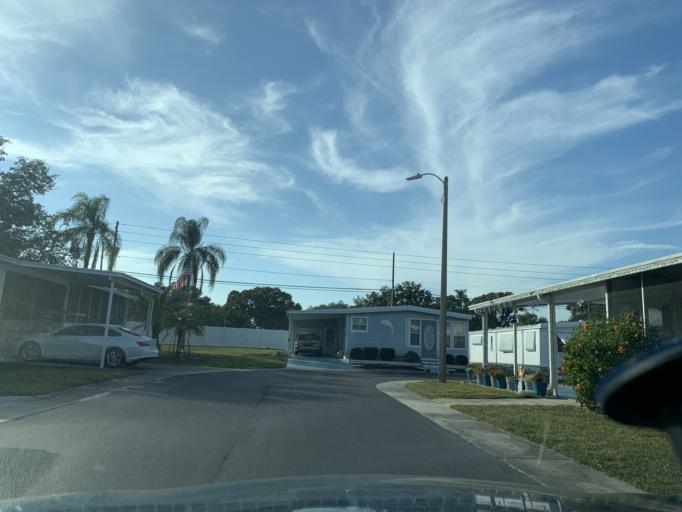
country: US
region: Florida
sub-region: Pinellas County
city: Ridgecrest
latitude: 27.8989
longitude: -82.7946
